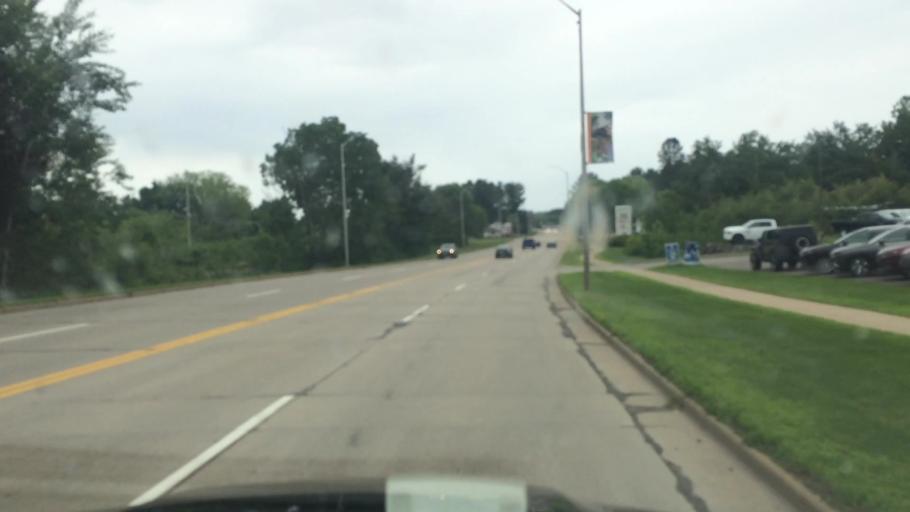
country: US
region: Wisconsin
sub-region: Lincoln County
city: Merrill
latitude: 45.1783
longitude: -89.6583
